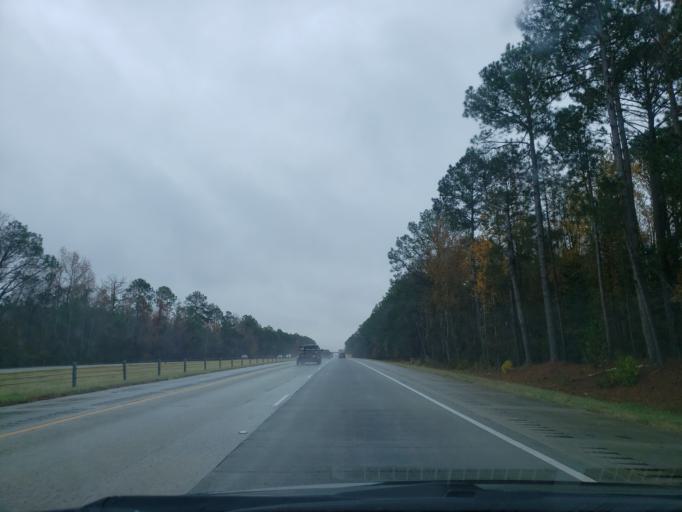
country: US
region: Georgia
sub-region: Treutlen County
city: Soperton
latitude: 32.4467
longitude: -82.7357
